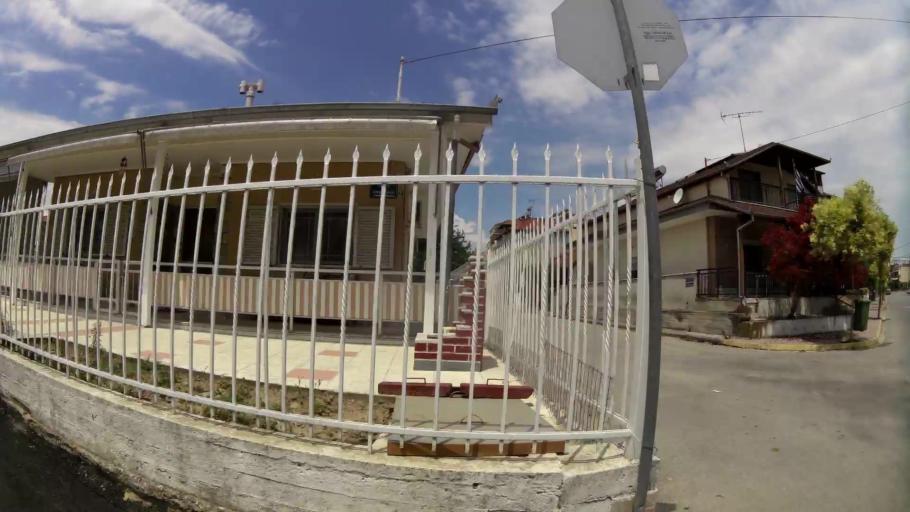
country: GR
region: Central Macedonia
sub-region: Nomos Pierias
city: Katerini
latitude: 40.2643
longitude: 22.5204
